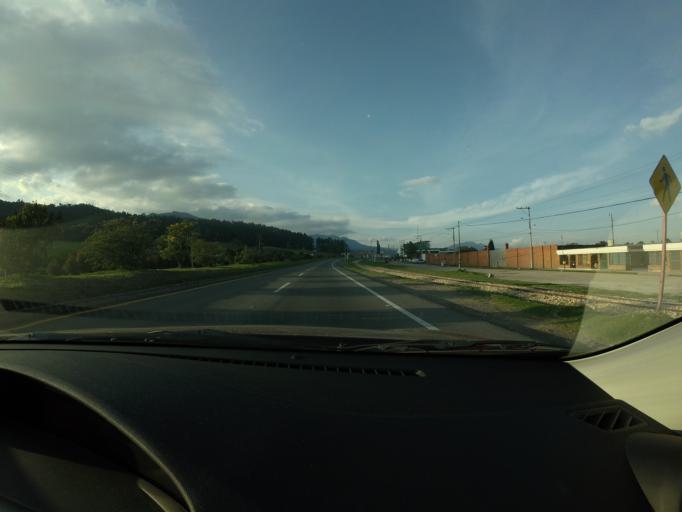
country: CO
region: Cundinamarca
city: Zipaquira
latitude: 5.0119
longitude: -74.0051
